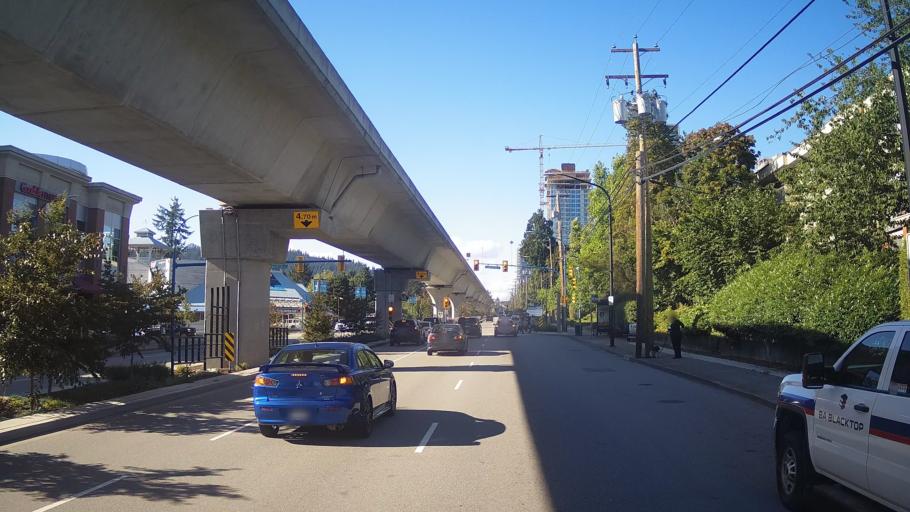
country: CA
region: British Columbia
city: New Westminster
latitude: 49.2525
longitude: -122.8929
